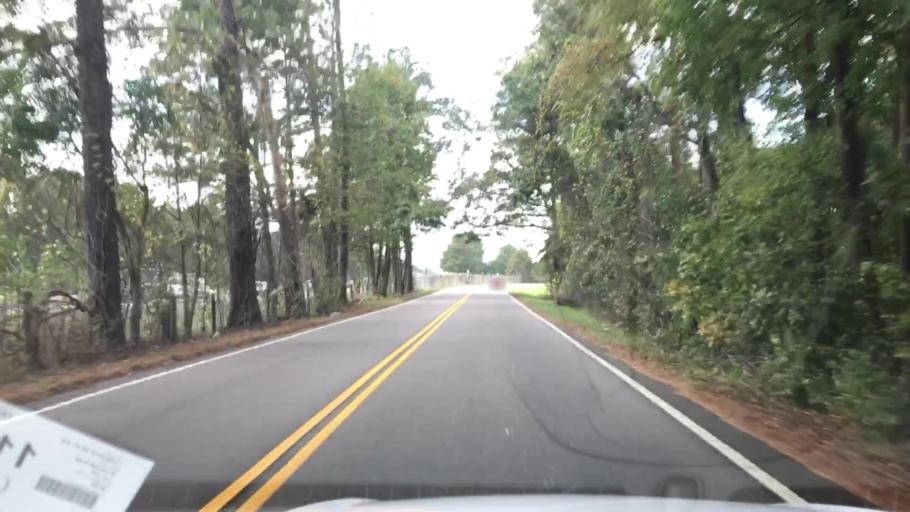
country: US
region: South Carolina
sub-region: Berkeley County
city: Ladson
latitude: 33.0080
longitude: -80.1061
